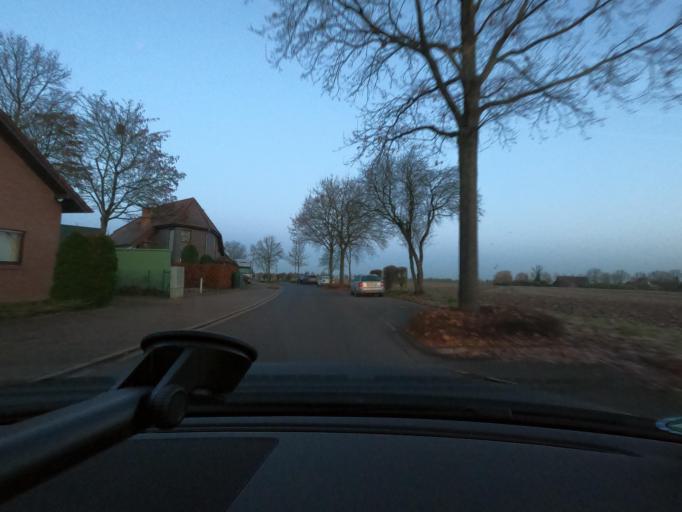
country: DE
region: North Rhine-Westphalia
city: Tonisvorst
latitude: 51.3288
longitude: 6.5001
